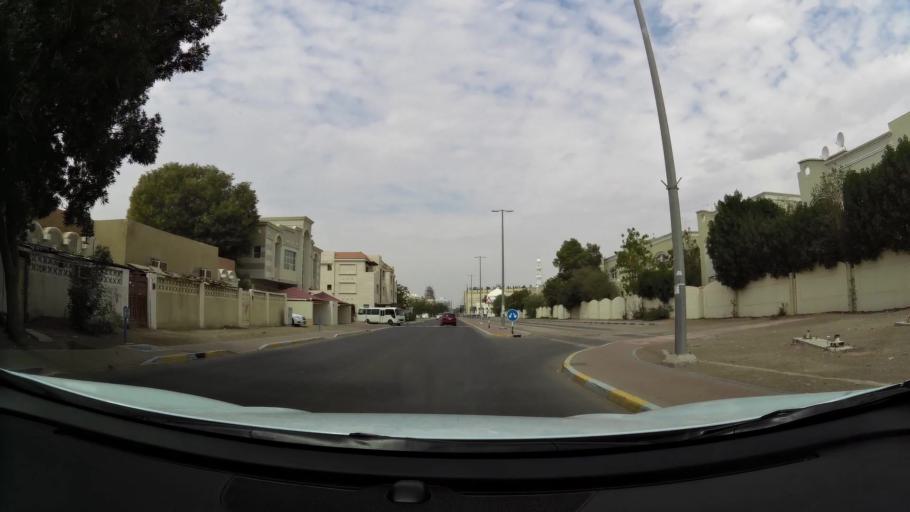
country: AE
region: Abu Dhabi
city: Al Ain
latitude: 24.2178
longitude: 55.7826
